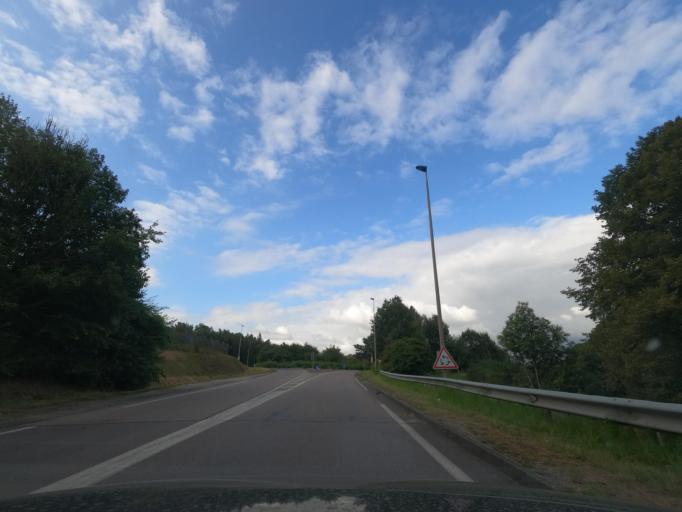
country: FR
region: Haute-Normandie
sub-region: Departement de l'Eure
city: Bernay
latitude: 49.0816
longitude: 0.5738
